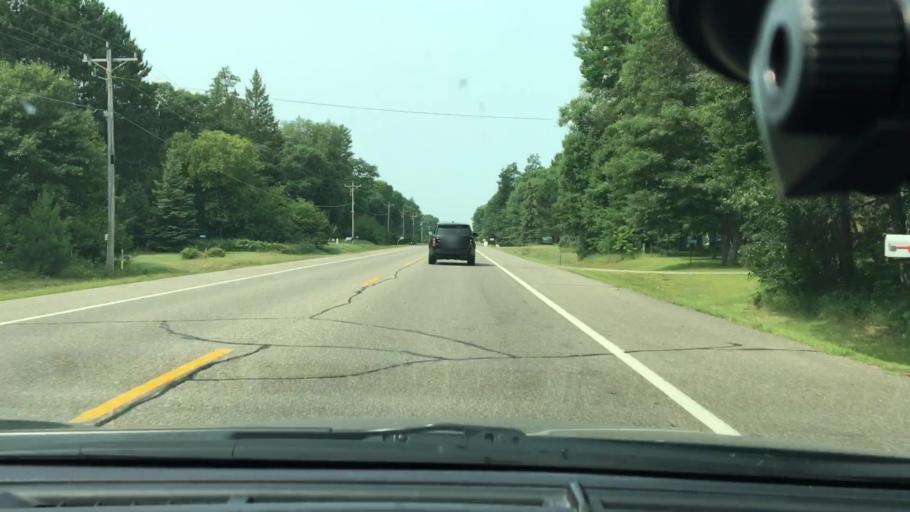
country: US
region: Minnesota
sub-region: Crow Wing County
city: Brainerd
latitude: 46.3985
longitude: -94.1967
